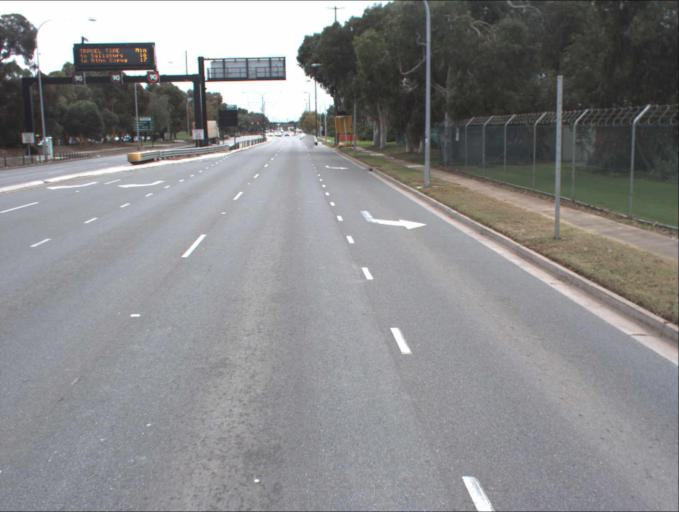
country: AU
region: South Australia
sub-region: Charles Sturt
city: Woodville
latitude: -34.8741
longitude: 138.5713
